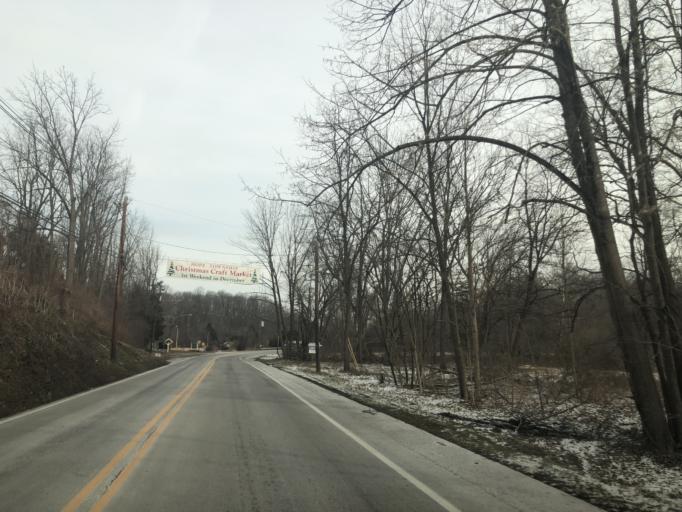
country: US
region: New Jersey
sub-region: Warren County
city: Oxford
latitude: 40.9188
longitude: -74.9663
